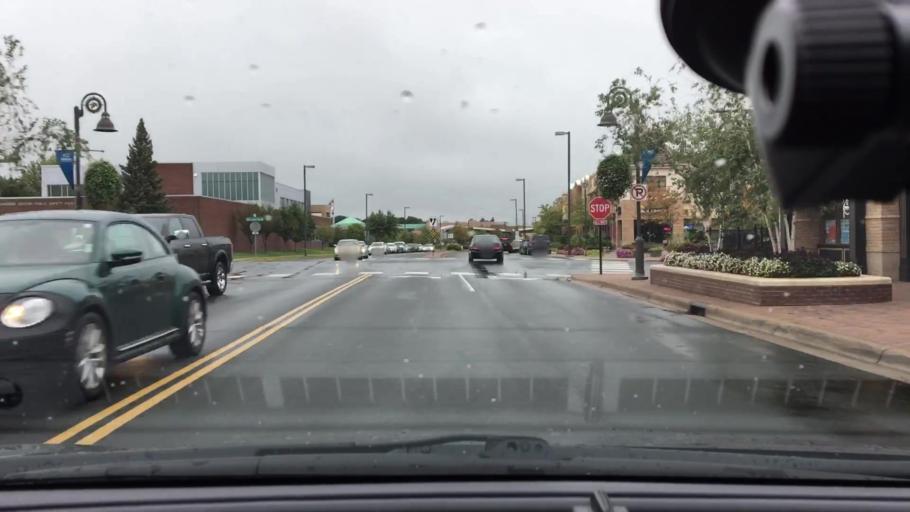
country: US
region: Minnesota
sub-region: Hennepin County
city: Maple Grove
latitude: 45.0979
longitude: -93.4417
